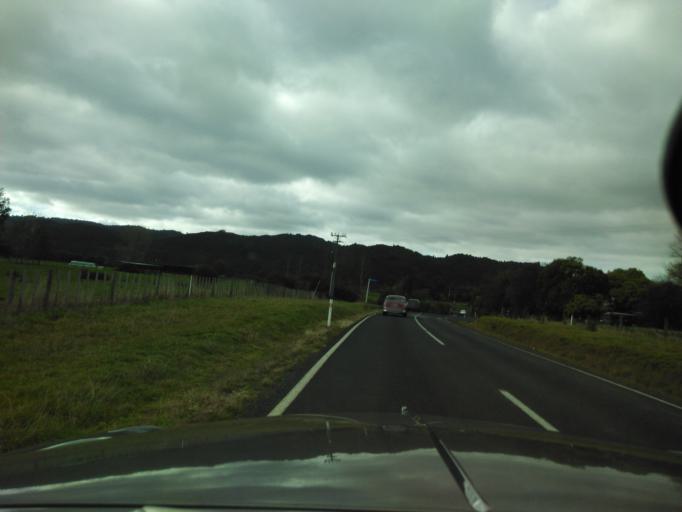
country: NZ
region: Auckland
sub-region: Auckland
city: Red Hill
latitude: -37.1090
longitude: 175.0879
